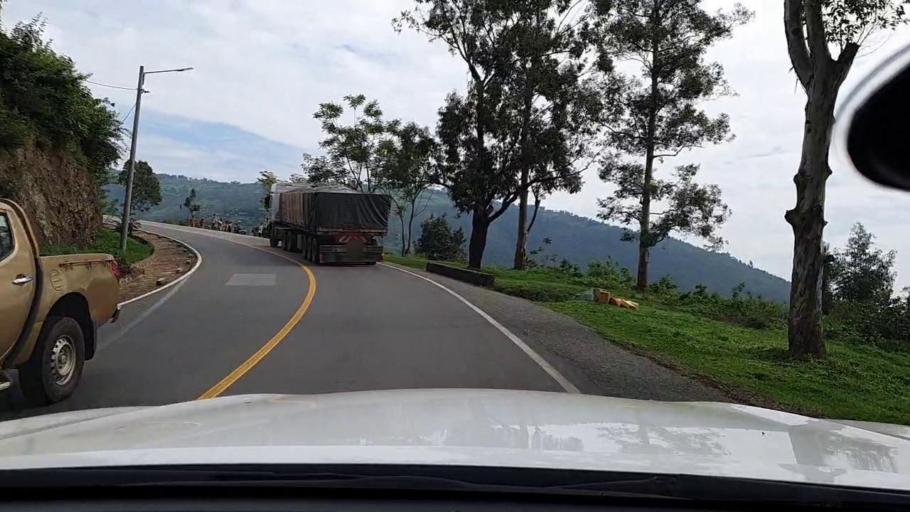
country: RW
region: Kigali
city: Kigali
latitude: -1.9422
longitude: 30.0294
